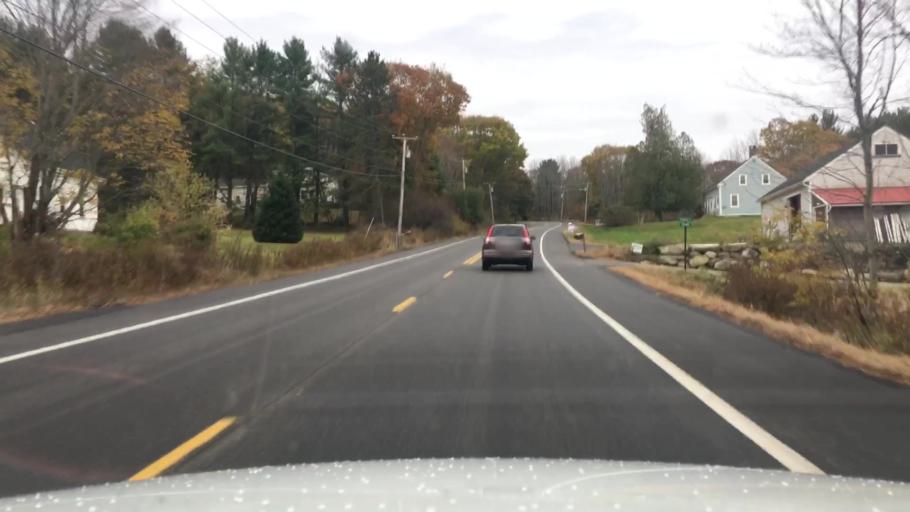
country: US
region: Maine
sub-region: Kennebec County
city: Pittston
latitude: 44.1851
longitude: -69.7460
